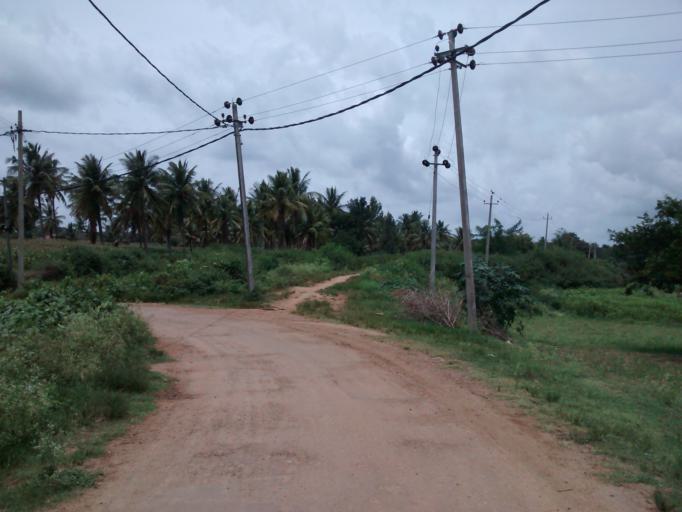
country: IN
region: Karnataka
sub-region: Hassan
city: Hassan
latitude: 12.9096
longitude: 76.1285
